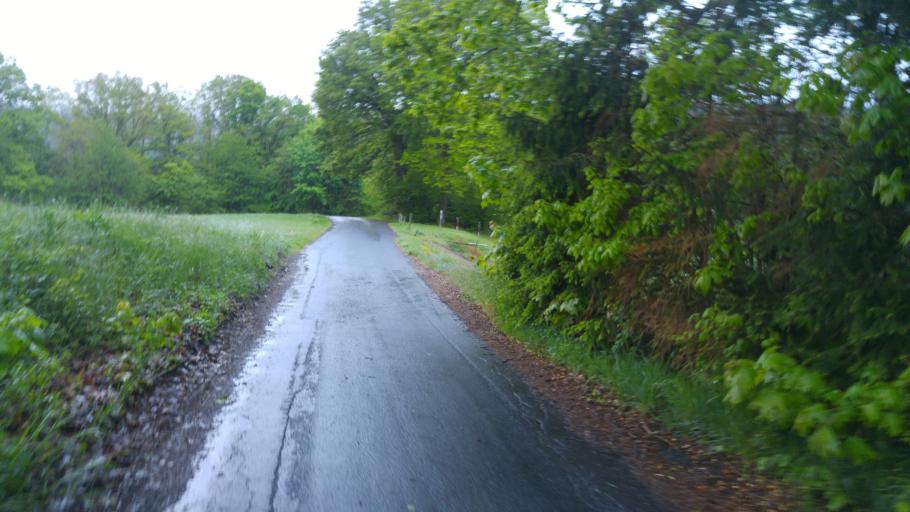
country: DE
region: Hesse
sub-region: Regierungsbezirk Darmstadt
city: Bad Orb
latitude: 50.2216
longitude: 9.3414
